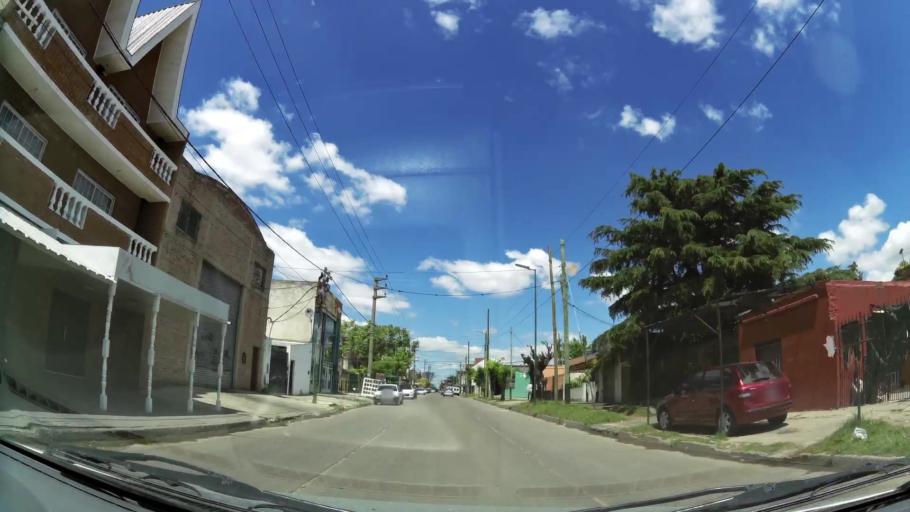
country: AR
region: Buenos Aires
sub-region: Partido de Lomas de Zamora
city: Lomas de Zamora
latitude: -34.7276
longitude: -58.4240
